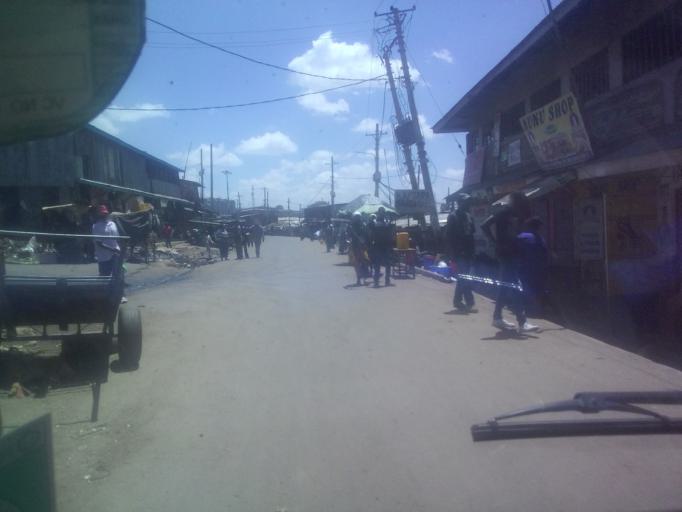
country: KE
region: Nairobi Area
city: Nairobi
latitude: -1.3153
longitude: 36.7973
